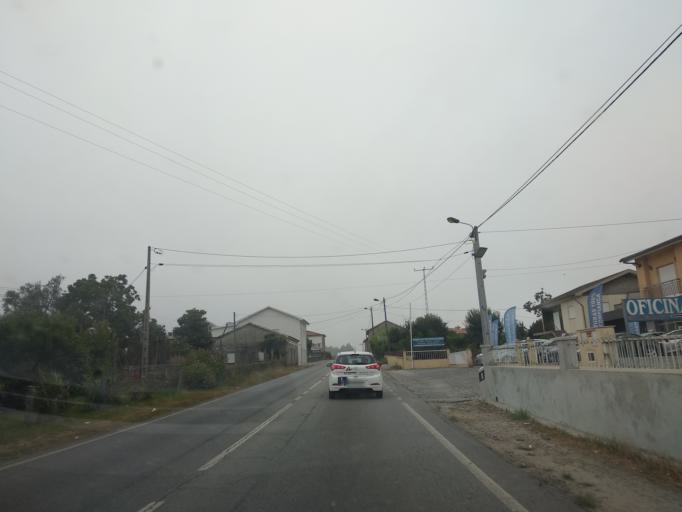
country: PT
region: Braga
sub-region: Vila Verde
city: Vila Verde
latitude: 41.6300
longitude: -8.4335
